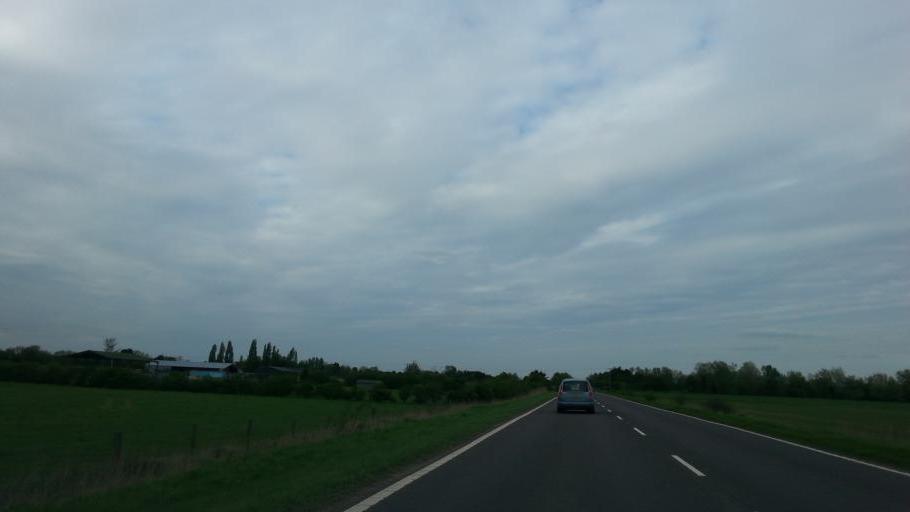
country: GB
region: England
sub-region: Cambridgeshire
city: Doddington
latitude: 52.4870
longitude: 0.0653
